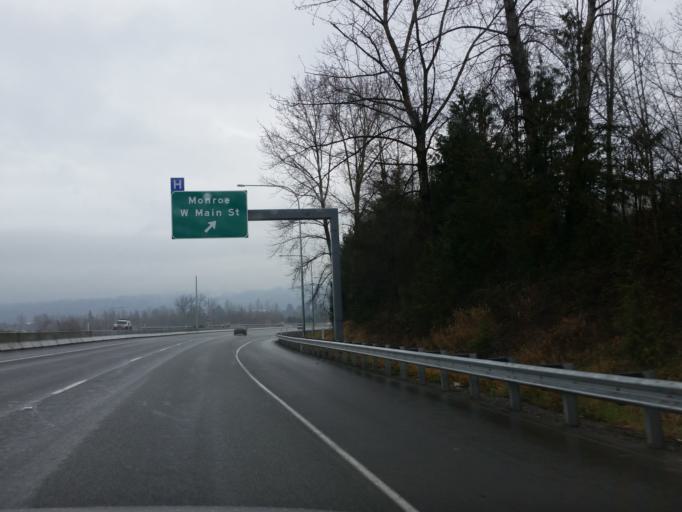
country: US
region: Washington
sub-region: Snohomish County
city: Monroe
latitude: 47.8457
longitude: -122.0116
